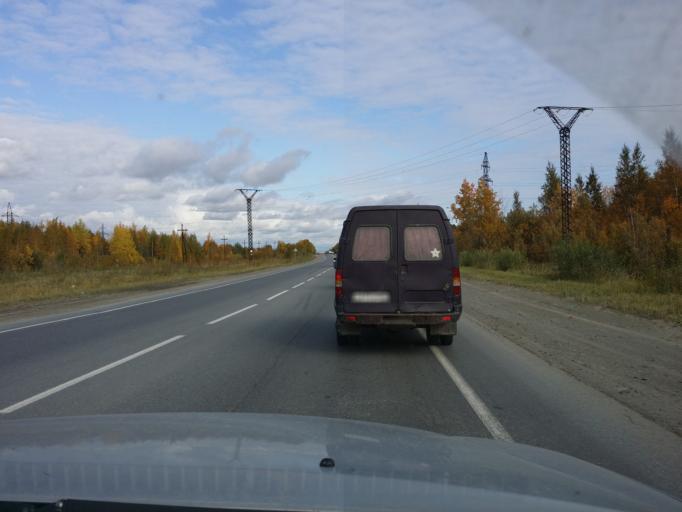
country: RU
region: Khanty-Mansiyskiy Avtonomnyy Okrug
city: Megion
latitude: 61.0583
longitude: 76.1143
